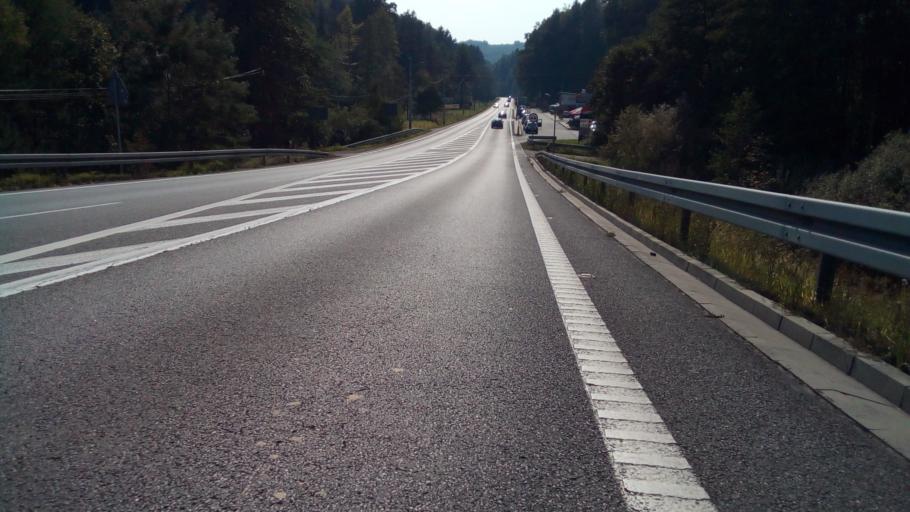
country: PL
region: Subcarpathian Voivodeship
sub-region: Powiat strzyzowski
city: Jawornik
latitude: 49.8326
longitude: 21.8836
